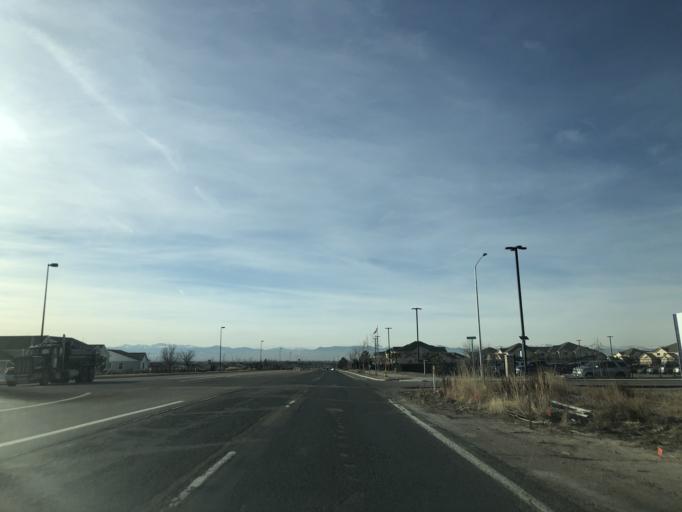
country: US
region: Colorado
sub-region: Adams County
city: Aurora
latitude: 39.7985
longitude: -104.7528
